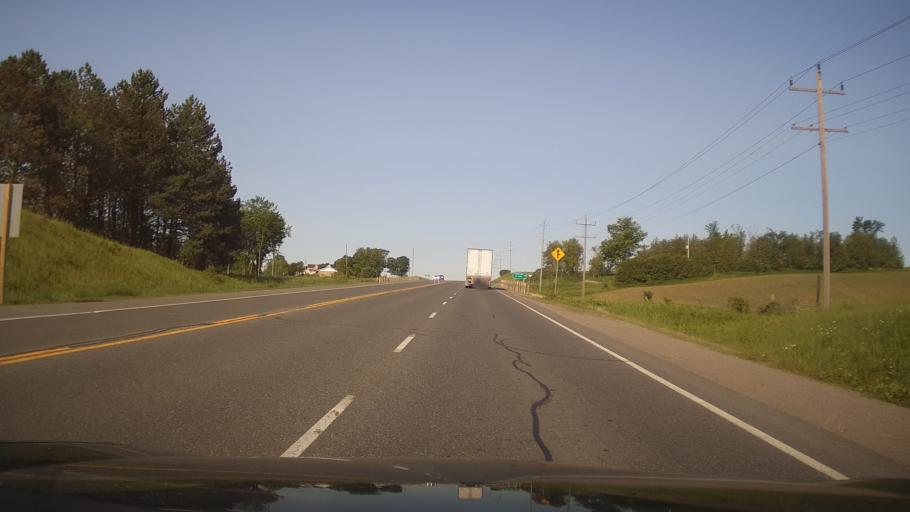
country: CA
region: Ontario
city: Peterborough
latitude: 44.3618
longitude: -78.0201
